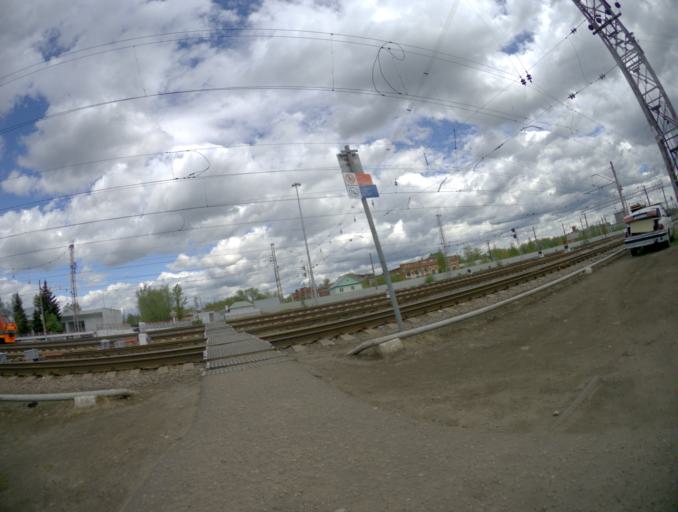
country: RU
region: Moskovskaya
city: Cherusti
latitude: 55.5416
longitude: 40.0050
